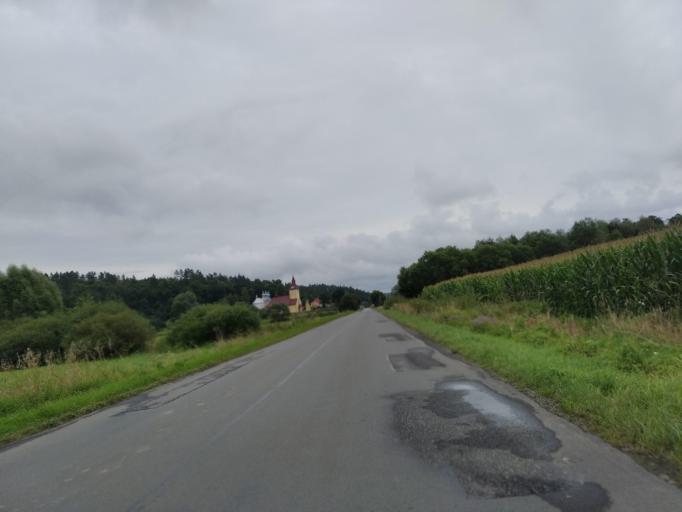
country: PL
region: Subcarpathian Voivodeship
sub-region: Powiat przemyski
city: Bircza
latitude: 49.7007
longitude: 22.3728
